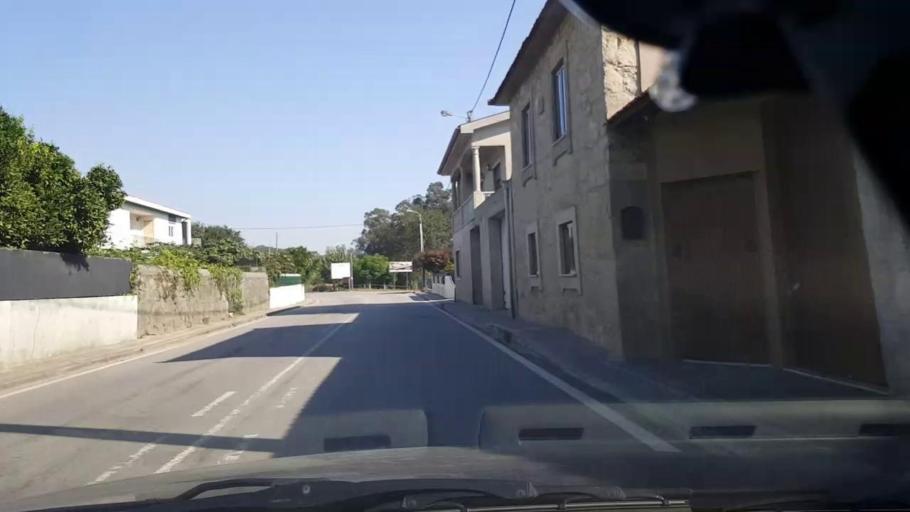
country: PT
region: Porto
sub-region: Vila do Conde
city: Arvore
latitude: 41.3473
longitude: -8.6788
